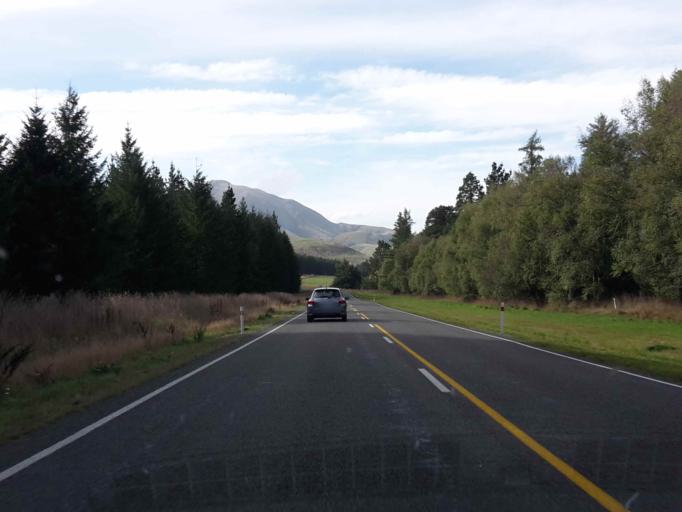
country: NZ
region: Canterbury
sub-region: Timaru District
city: Pleasant Point
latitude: -44.0459
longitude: 170.6831
